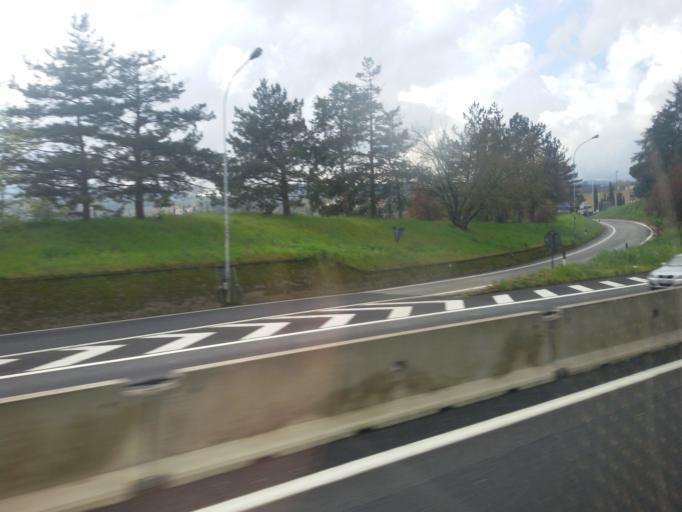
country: IT
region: Tuscany
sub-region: Province of Florence
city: Incisa in Val d'Arno
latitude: 43.6628
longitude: 11.4607
